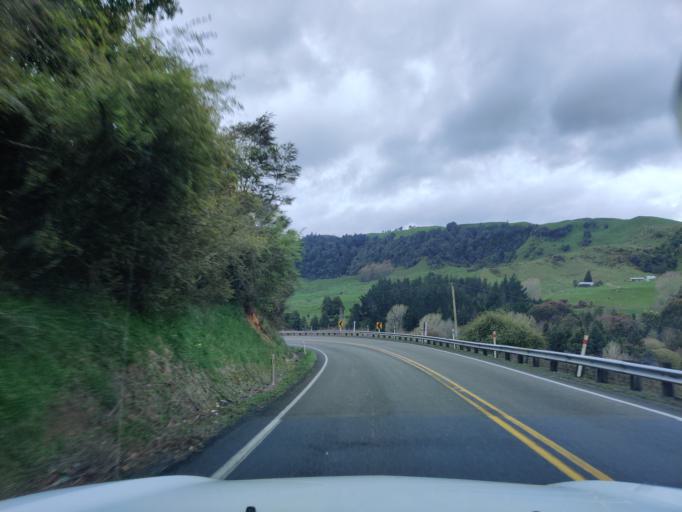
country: NZ
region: Waikato
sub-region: Otorohanga District
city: Otorohanga
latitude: -38.4927
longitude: 175.1890
